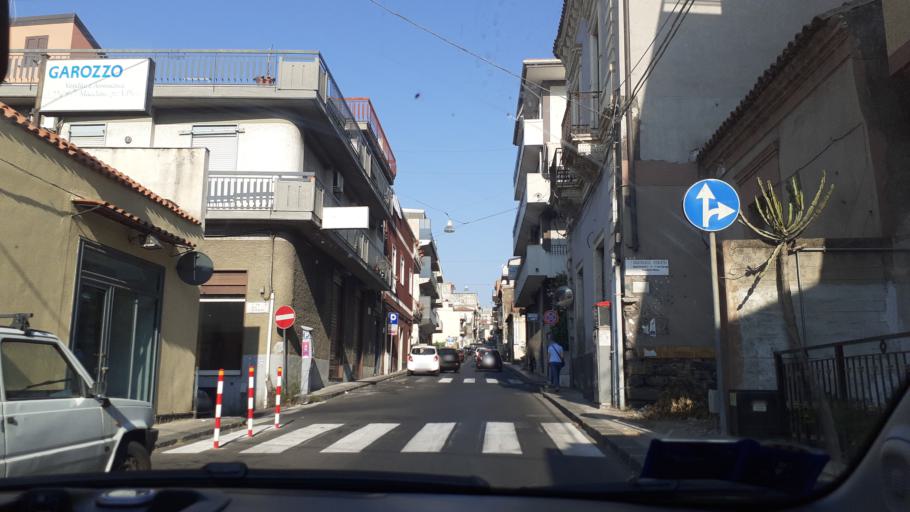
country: IT
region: Sicily
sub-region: Catania
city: Misterbianco
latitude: 37.5174
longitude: 15.0128
